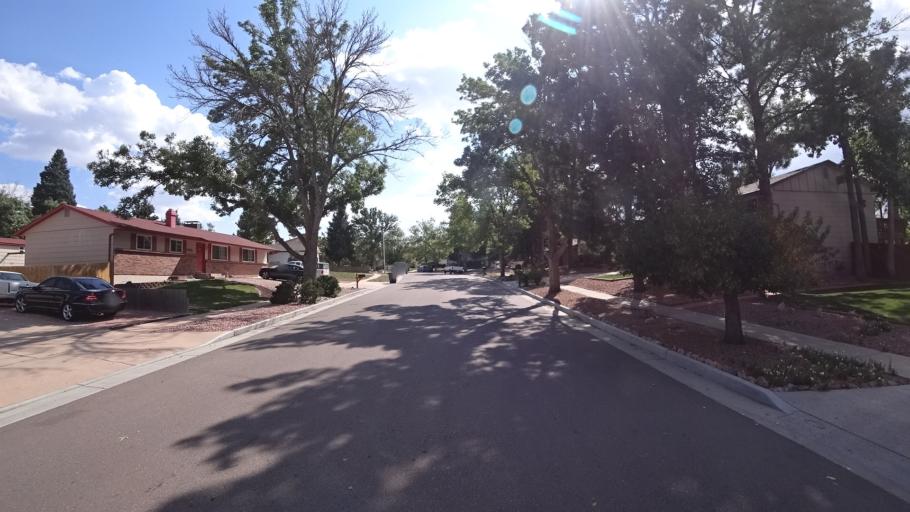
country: US
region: Colorado
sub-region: El Paso County
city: Cimarron Hills
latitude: 38.8776
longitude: -104.7341
